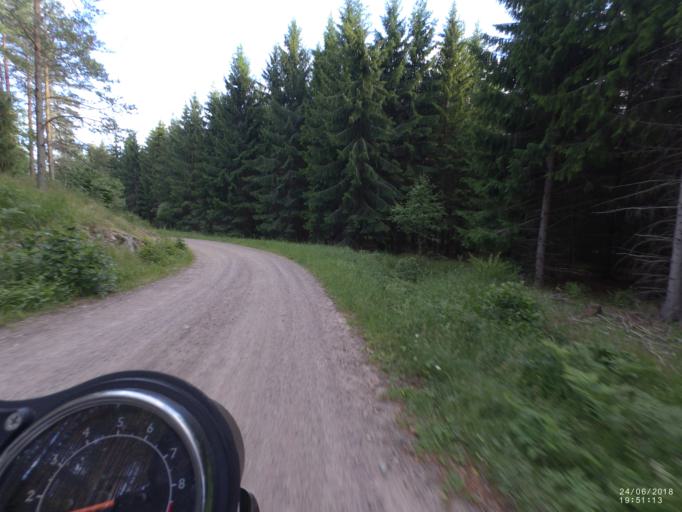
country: SE
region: Soedermanland
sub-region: Oxelosunds Kommun
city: Oxelosund
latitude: 58.7734
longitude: 17.1516
